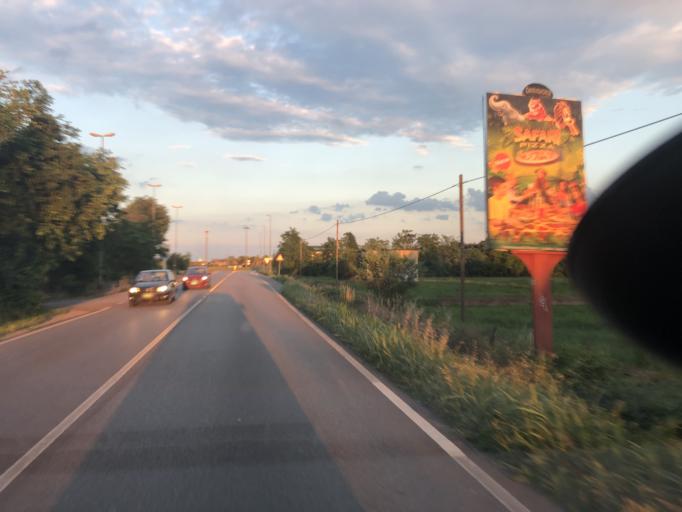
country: IT
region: Veneto
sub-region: Provincia di Verona
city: Pescantina
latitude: 45.4933
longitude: 10.8788
